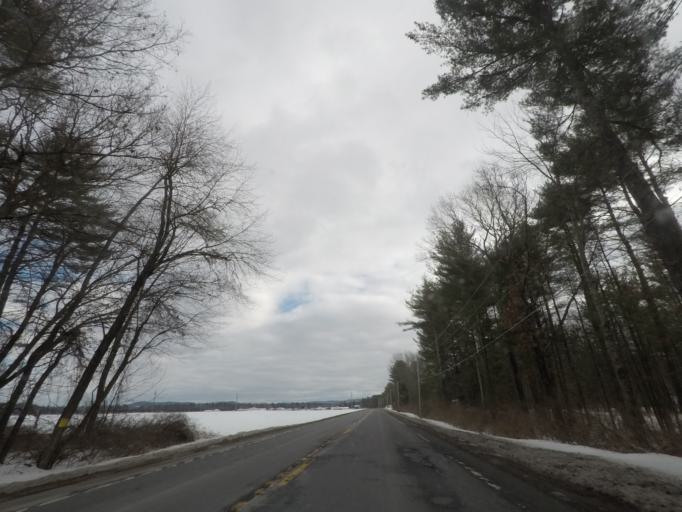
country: US
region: New York
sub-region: Saratoga County
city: Schuylerville
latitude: 43.0939
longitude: -73.5573
